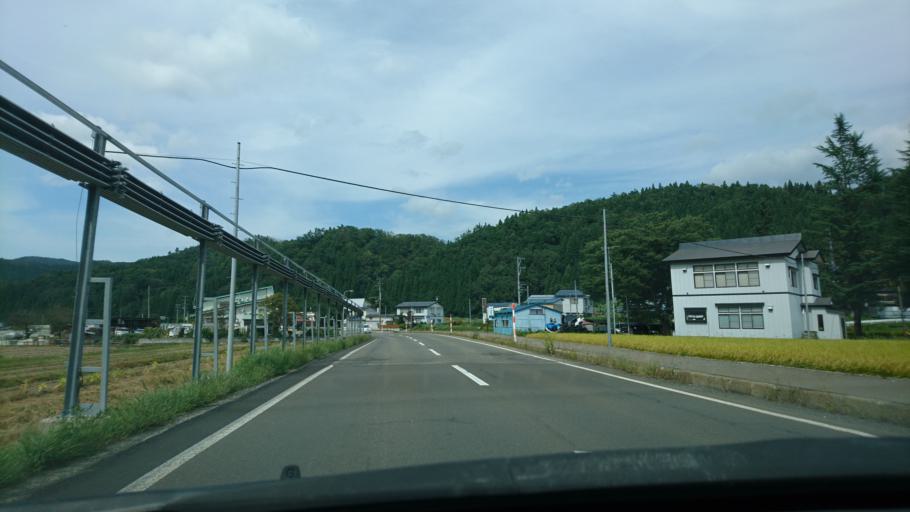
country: JP
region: Akita
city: Yuzawa
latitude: 39.1919
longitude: 140.6185
